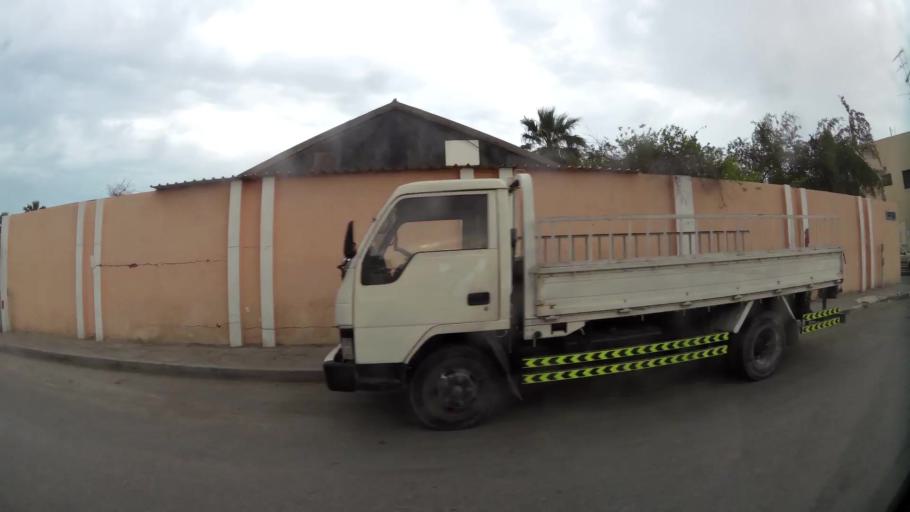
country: QA
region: Baladiyat ad Dawhah
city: Doha
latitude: 25.2708
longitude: 51.5047
